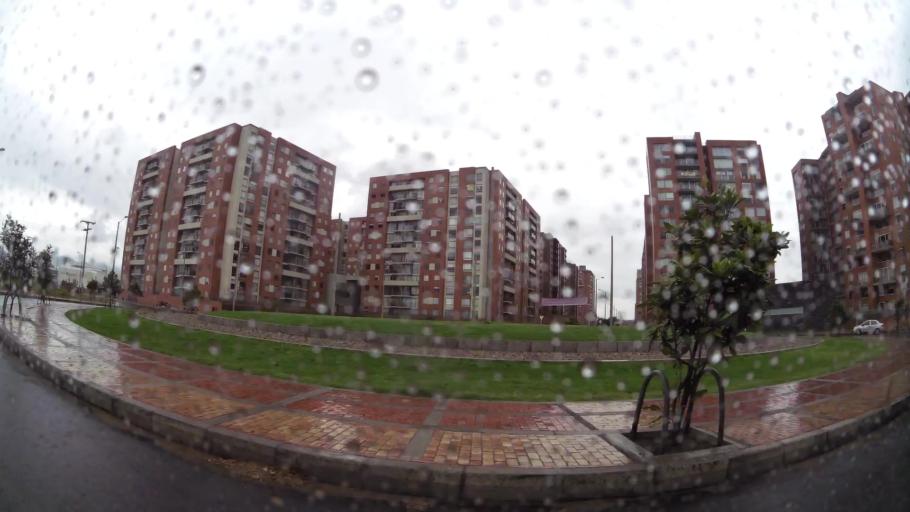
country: CO
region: Bogota D.C.
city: Bogota
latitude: 4.6573
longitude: -74.1280
